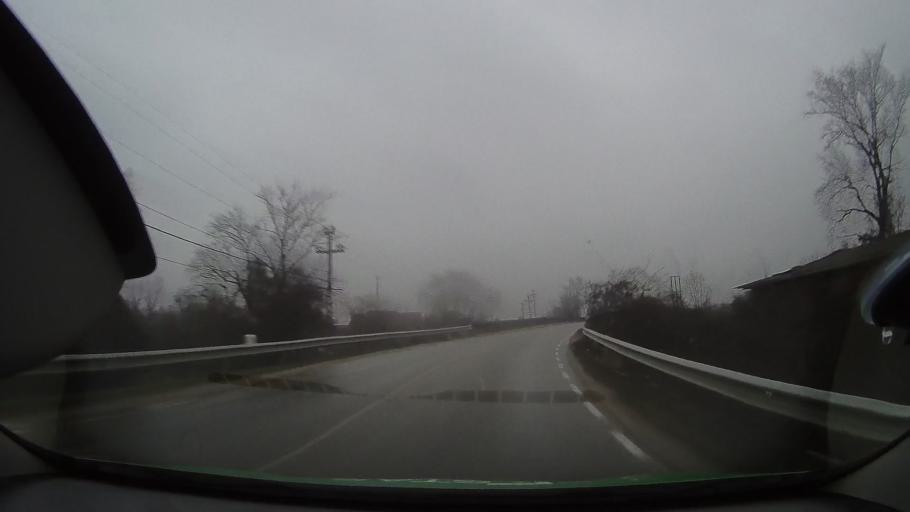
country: RO
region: Bihor
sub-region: Comuna Tinca
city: Tinca
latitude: 46.7692
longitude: 21.9325
